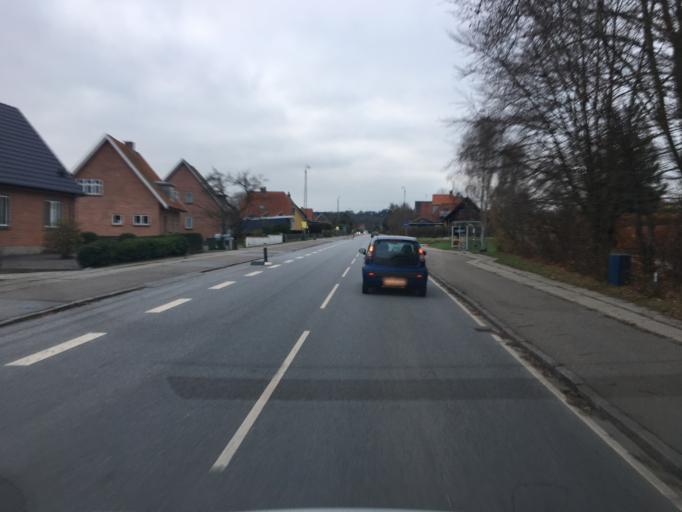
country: DK
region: South Denmark
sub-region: Aabenraa Kommune
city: Aabenraa
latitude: 55.0340
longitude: 9.3921
